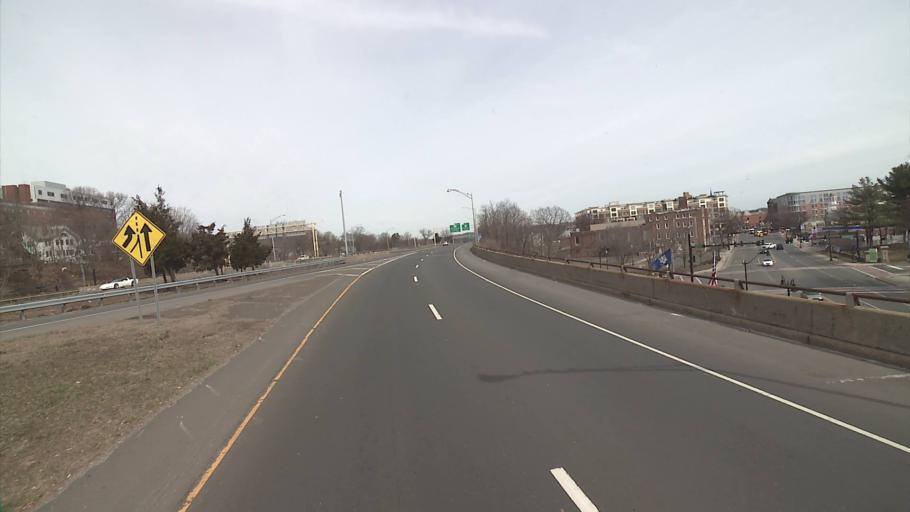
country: US
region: Connecticut
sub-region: Fairfield County
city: Norwalk
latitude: 41.1093
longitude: -73.4187
